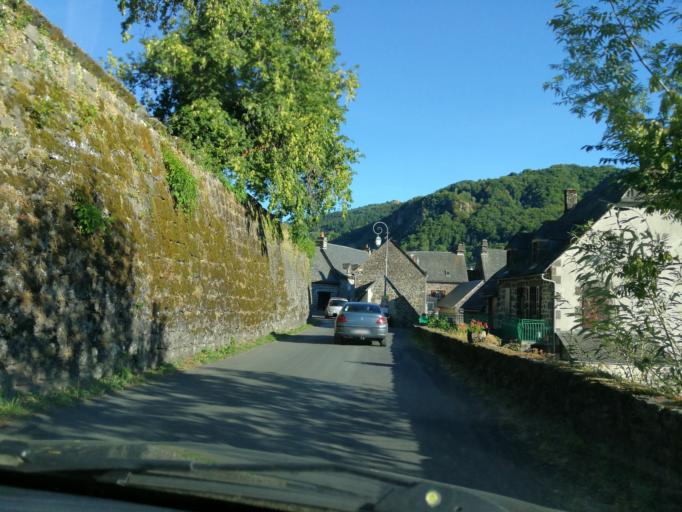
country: FR
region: Auvergne
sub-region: Departement du Cantal
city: Saint-Cernin
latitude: 45.1147
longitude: 2.5029
